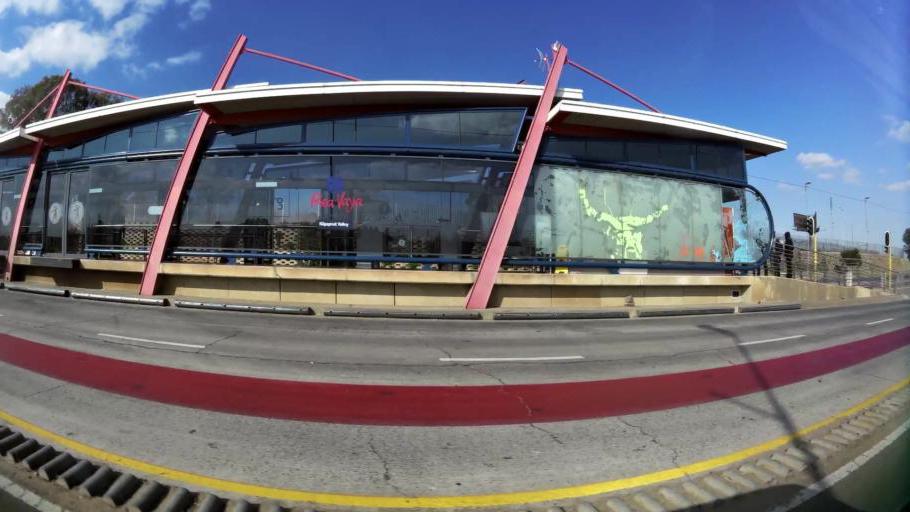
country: ZA
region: Gauteng
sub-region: City of Johannesburg Metropolitan Municipality
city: Soweto
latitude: -26.2609
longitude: 27.8906
